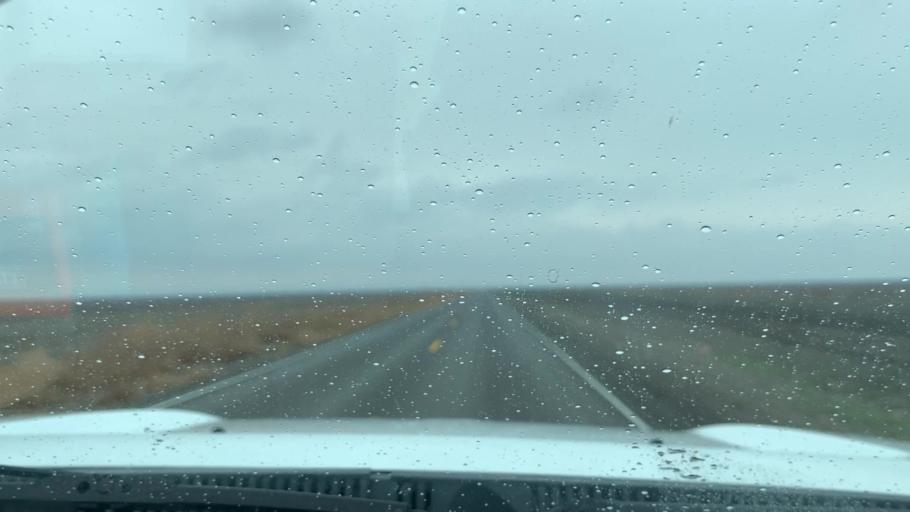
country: US
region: California
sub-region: Kings County
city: Corcoran
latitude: 35.9341
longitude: -119.7228
